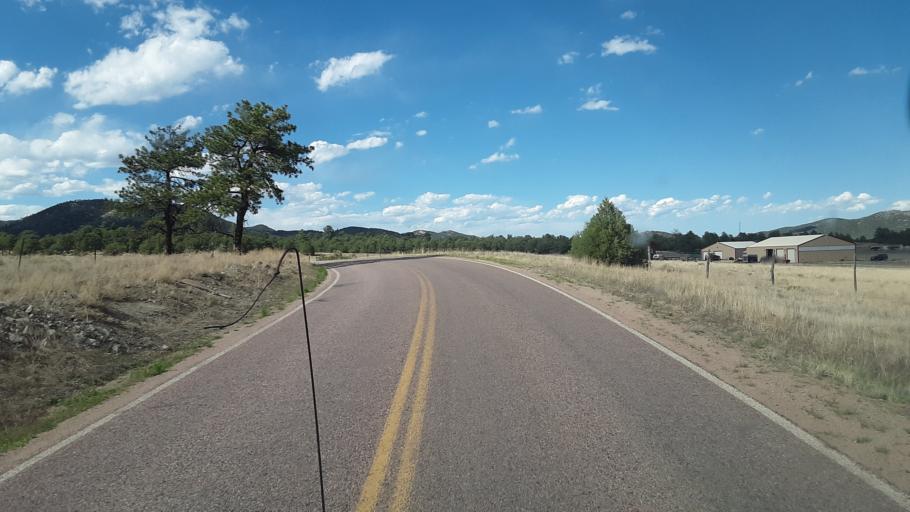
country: US
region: Colorado
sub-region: Custer County
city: Westcliffe
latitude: 38.3529
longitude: -105.4816
